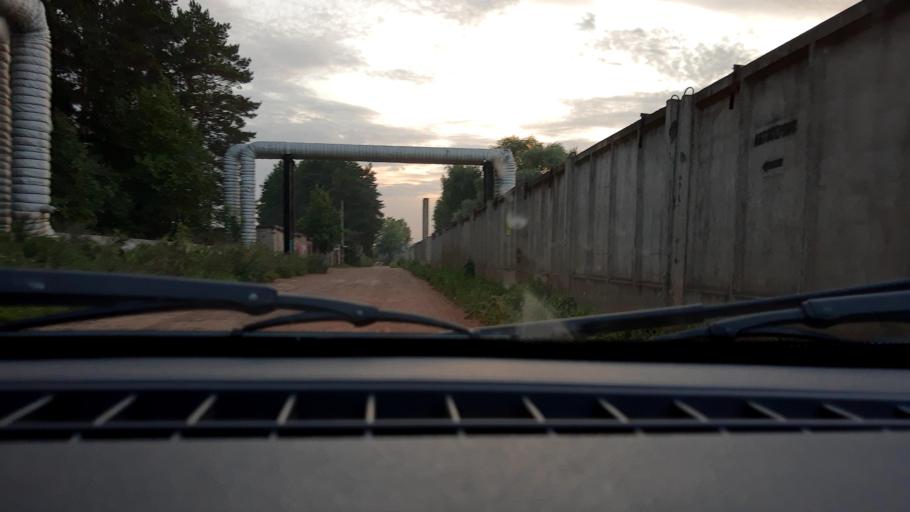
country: RU
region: Bashkortostan
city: Mikhaylovka
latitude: 54.7898
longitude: 55.8599
